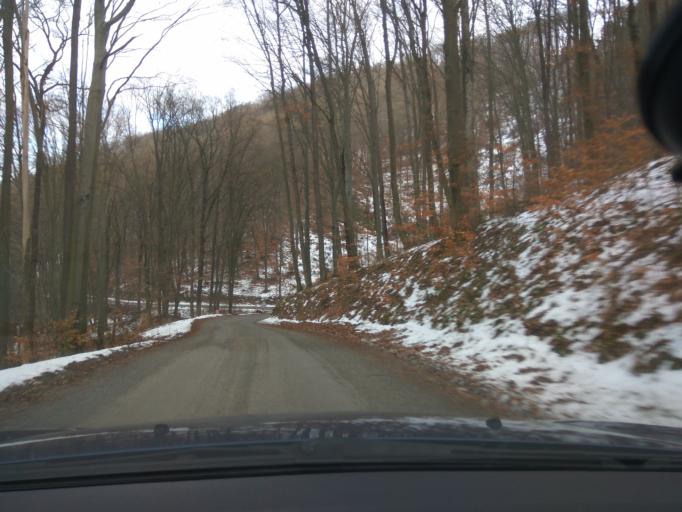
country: SK
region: Banskobystricky
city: Zarnovica
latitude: 48.4728
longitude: 18.7335
